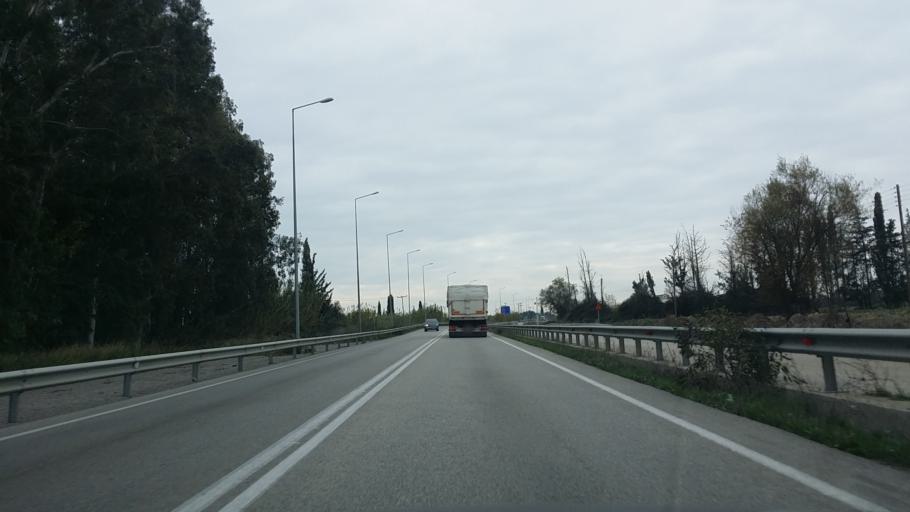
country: GR
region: West Greece
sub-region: Nomos Aitolias kai Akarnanias
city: Mesolongi
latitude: 38.3793
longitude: 21.4841
